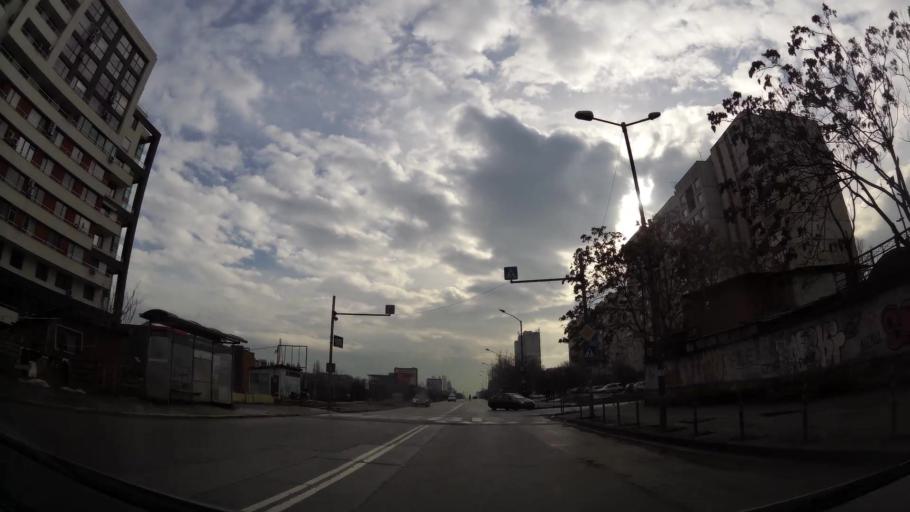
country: BG
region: Sofiya
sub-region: Obshtina Bozhurishte
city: Bozhurishte
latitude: 42.7233
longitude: 23.2481
